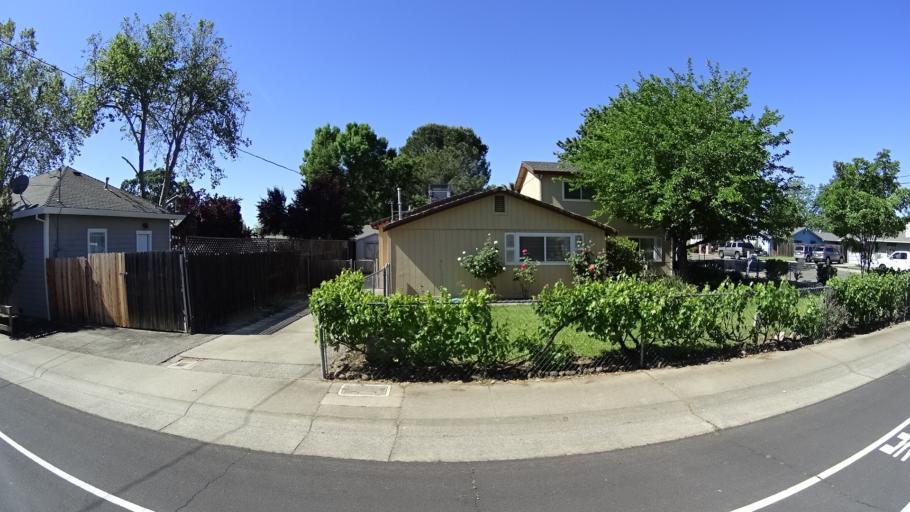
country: US
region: California
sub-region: Placer County
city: Rocklin
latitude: 38.7925
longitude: -121.2404
